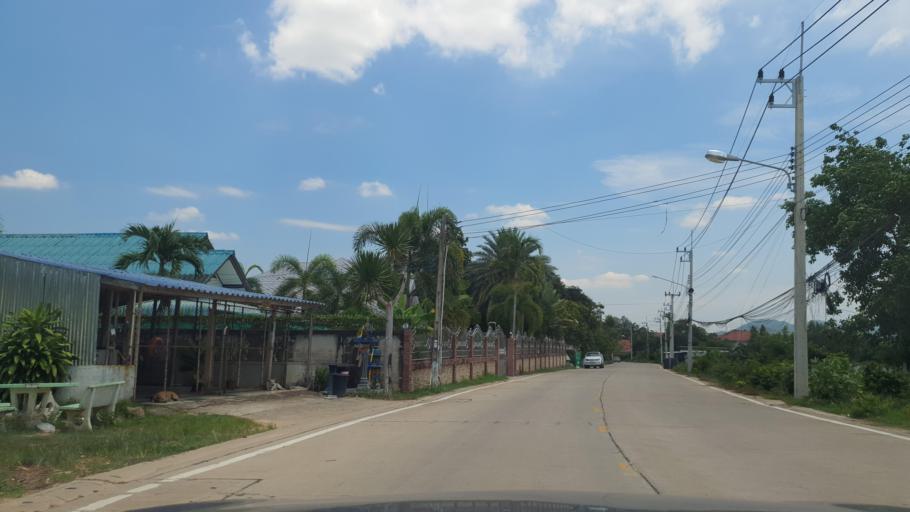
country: TH
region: Chon Buri
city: Phatthaya
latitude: 12.8138
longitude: 100.9386
